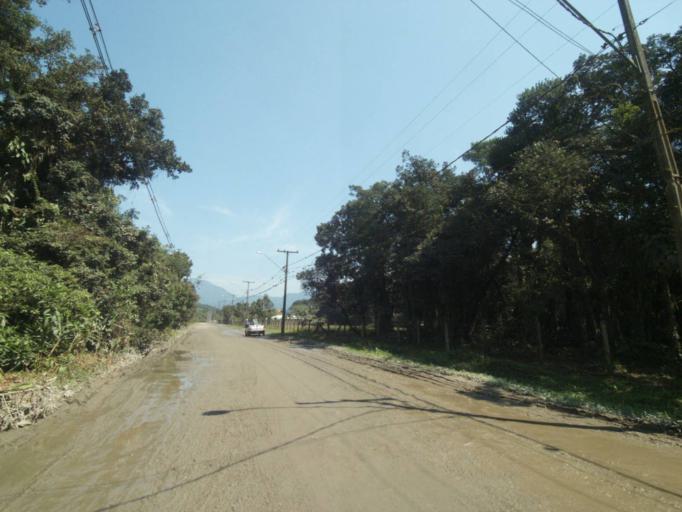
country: BR
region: Parana
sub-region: Paranagua
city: Paranagua
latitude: -25.5508
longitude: -48.5865
